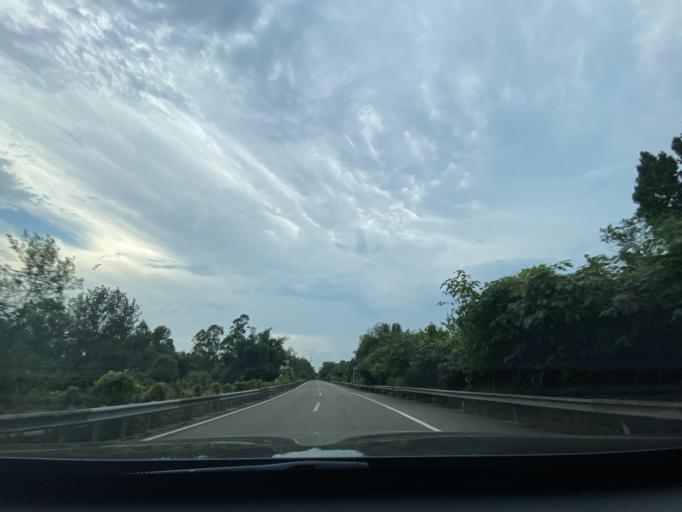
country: CN
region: Sichuan
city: Neijiang
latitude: 29.6788
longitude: 104.9662
